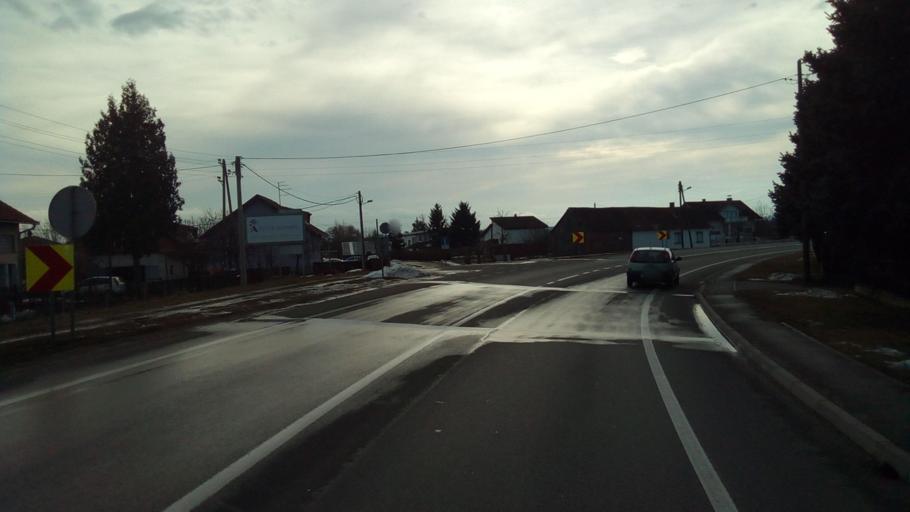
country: HR
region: Varazdinska
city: Jalzabet
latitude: 46.2991
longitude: 16.4459
